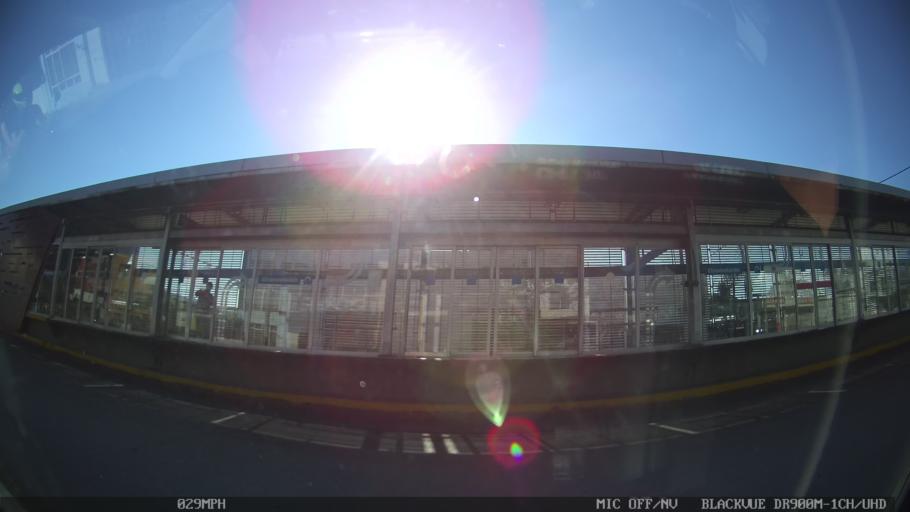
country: MX
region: Jalisco
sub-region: Zapopan
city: Zapopan
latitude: 20.6948
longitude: -103.3312
